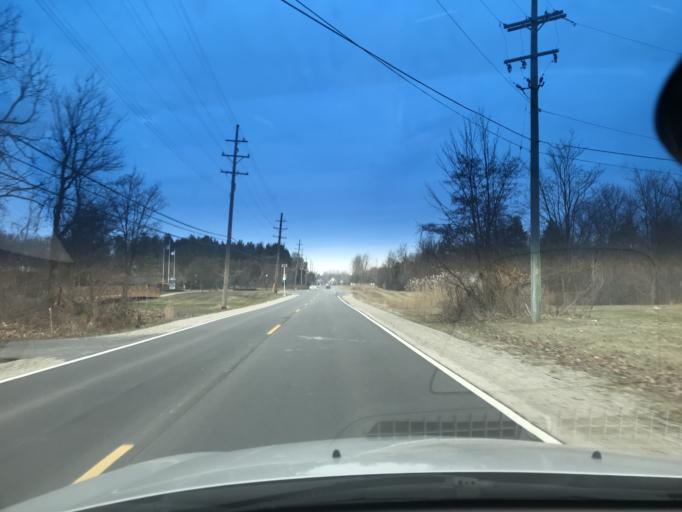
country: US
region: Michigan
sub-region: Macomb County
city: Shelby
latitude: 42.7052
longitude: -83.0540
